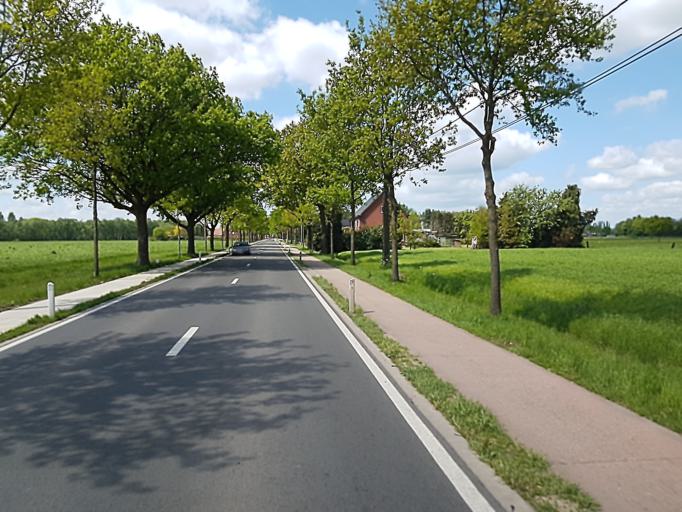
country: BE
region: Flanders
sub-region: Provincie Antwerpen
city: Rijkevorsel
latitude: 51.3486
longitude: 4.7318
